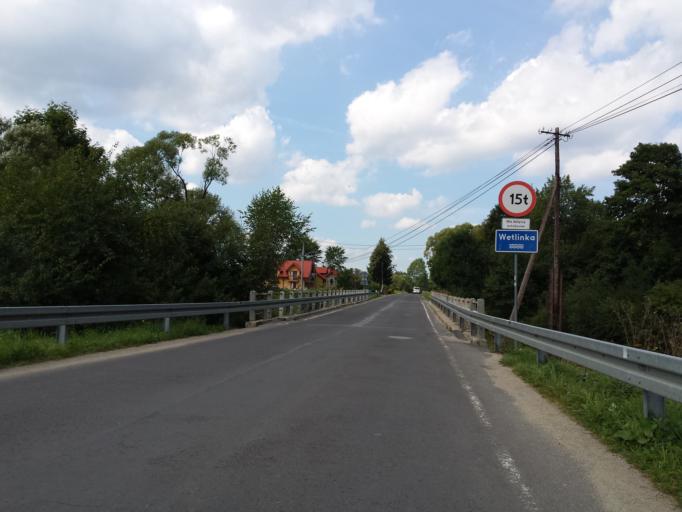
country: PL
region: Subcarpathian Voivodeship
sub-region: Powiat leski
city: Cisna
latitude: 49.1511
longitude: 22.4736
